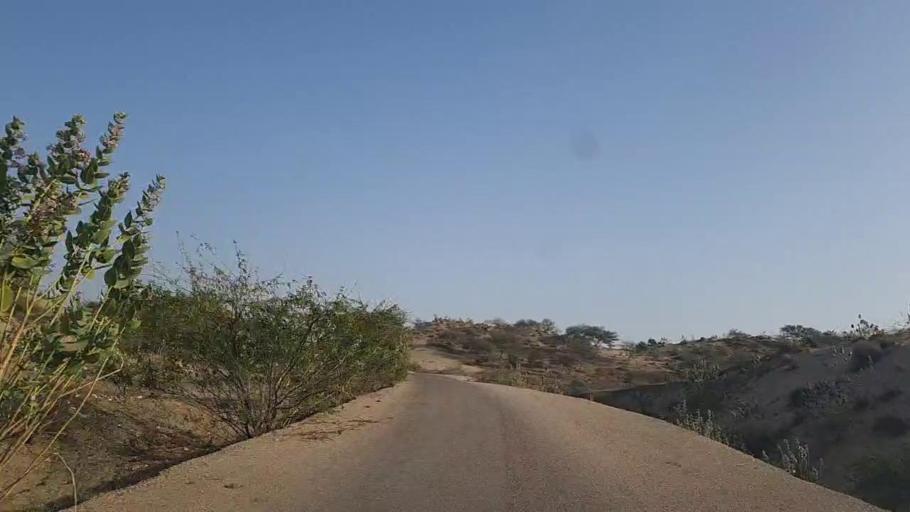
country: PK
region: Sindh
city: Diplo
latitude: 24.6016
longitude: 69.3810
